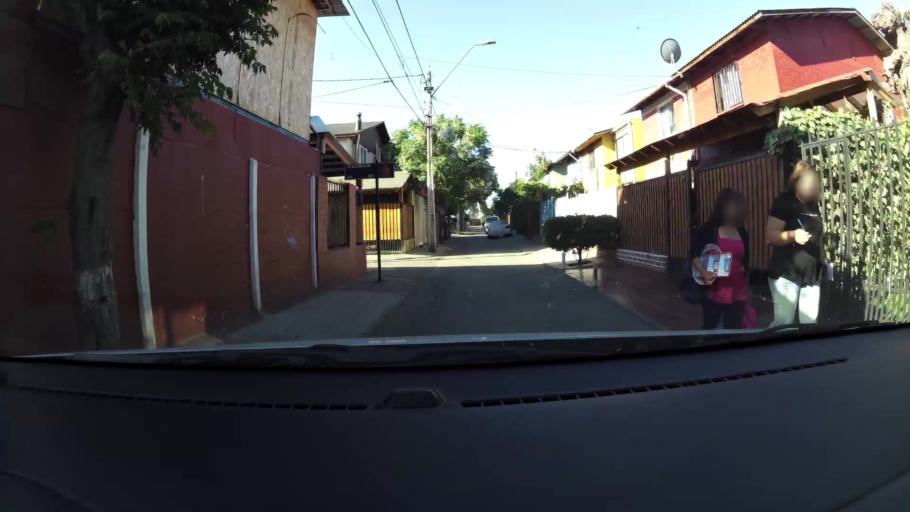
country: CL
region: Santiago Metropolitan
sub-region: Provincia de Maipo
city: San Bernardo
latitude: -33.6020
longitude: -70.6807
